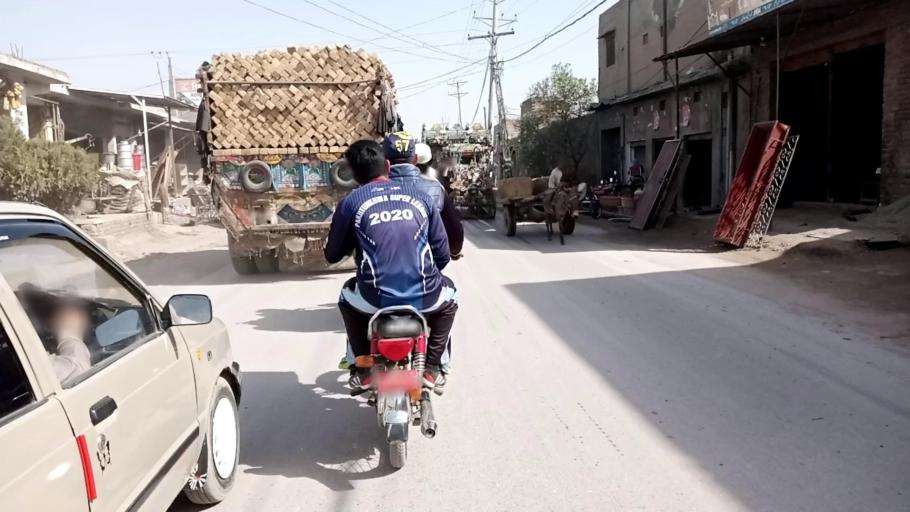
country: PK
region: Khyber Pakhtunkhwa
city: Peshawar
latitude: 34.0081
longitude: 71.6438
